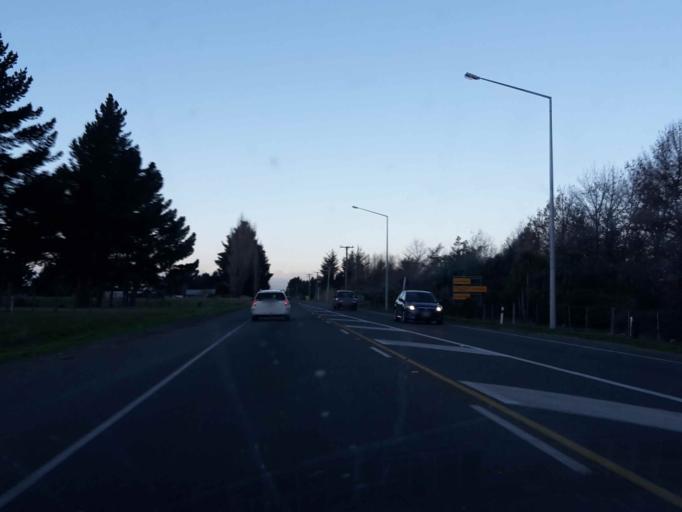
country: NZ
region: Canterbury
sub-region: Selwyn District
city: Rolleston
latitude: -43.5669
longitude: 172.4452
